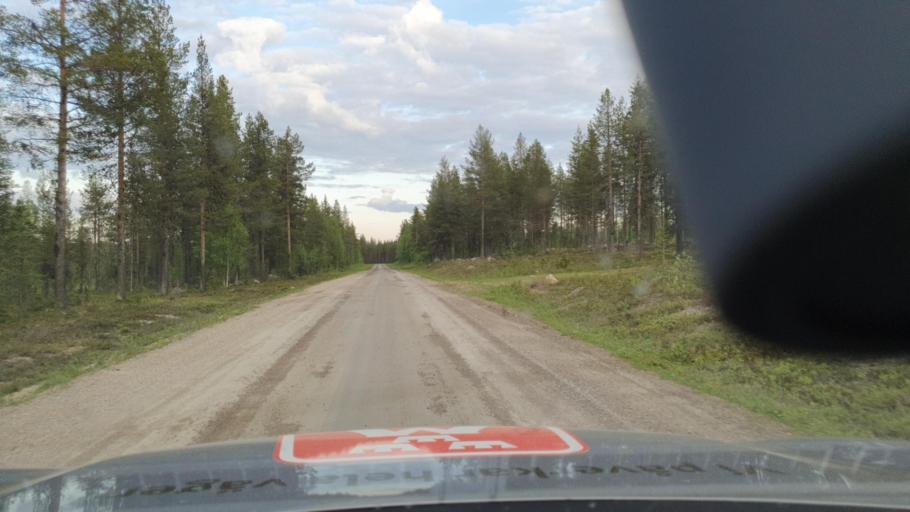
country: SE
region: Norrbotten
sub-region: Gallivare Kommun
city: Gaellivare
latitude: 66.7042
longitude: 21.1607
